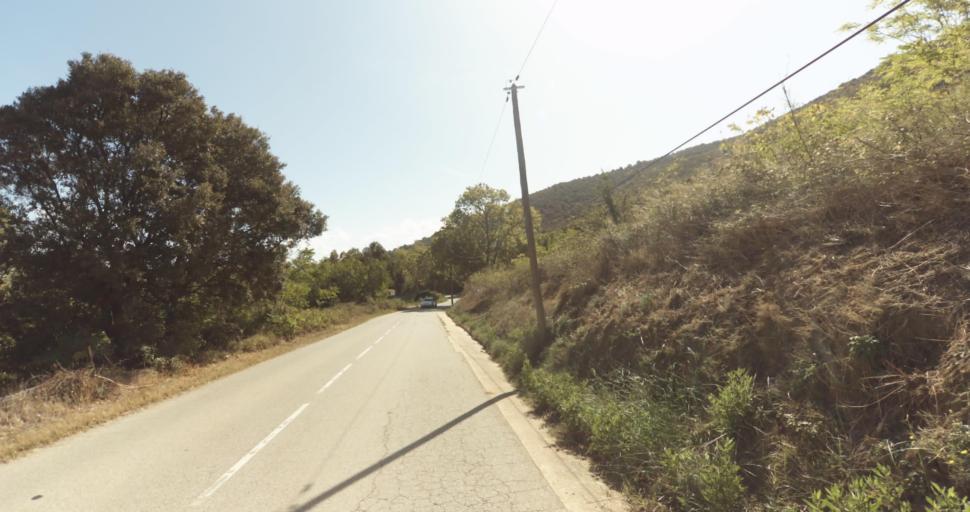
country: FR
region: Corsica
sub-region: Departement de la Corse-du-Sud
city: Ajaccio
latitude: 41.9292
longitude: 8.6986
